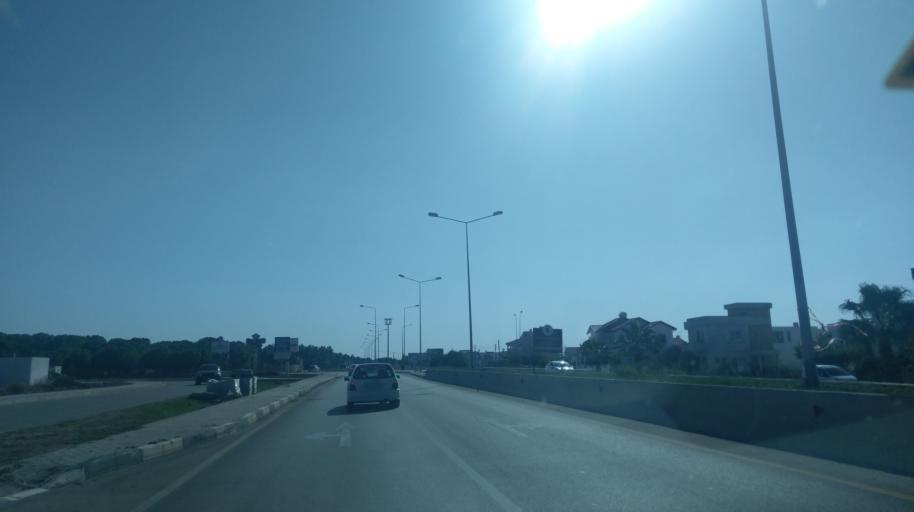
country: CY
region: Ammochostos
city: Trikomo
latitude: 35.2063
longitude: 33.8940
